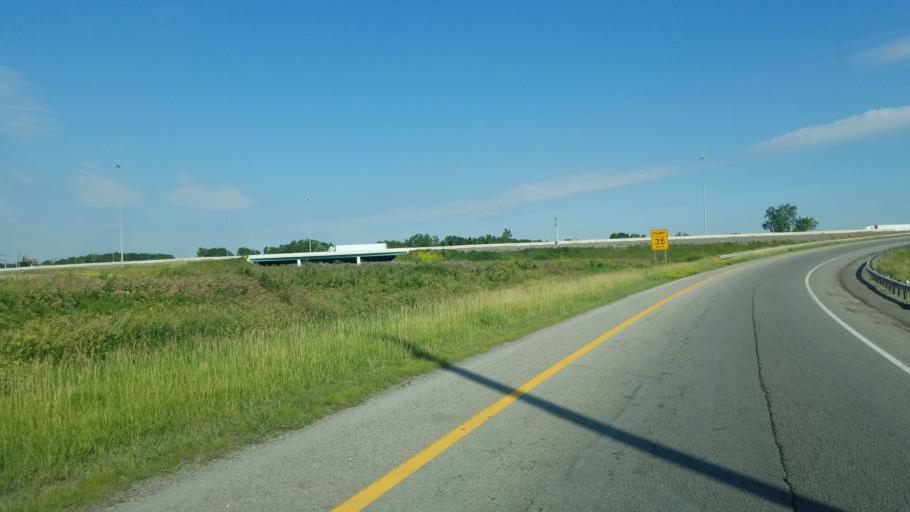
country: US
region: Ohio
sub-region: Hancock County
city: Findlay
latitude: 41.0257
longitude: -83.6714
